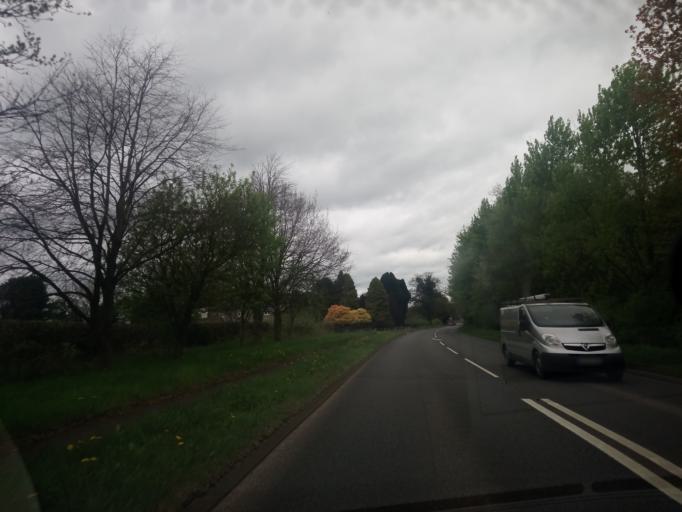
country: GB
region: England
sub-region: Shropshire
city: Stoke upon Tern
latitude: 52.8436
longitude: -2.4688
